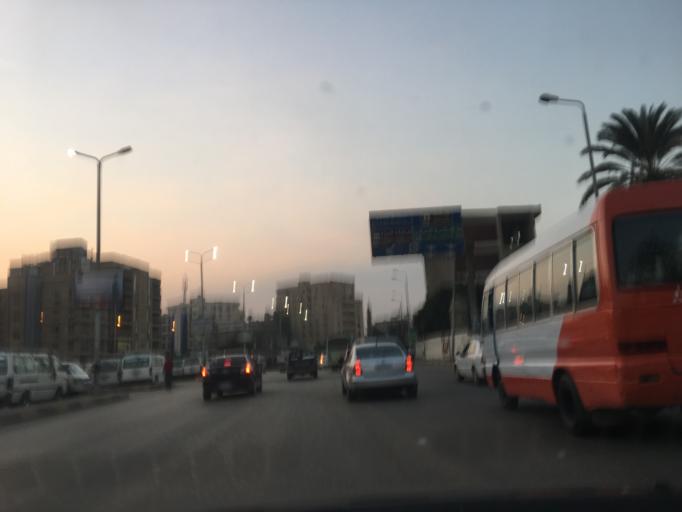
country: EG
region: Al Jizah
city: Al Jizah
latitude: 29.9907
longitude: 31.1322
